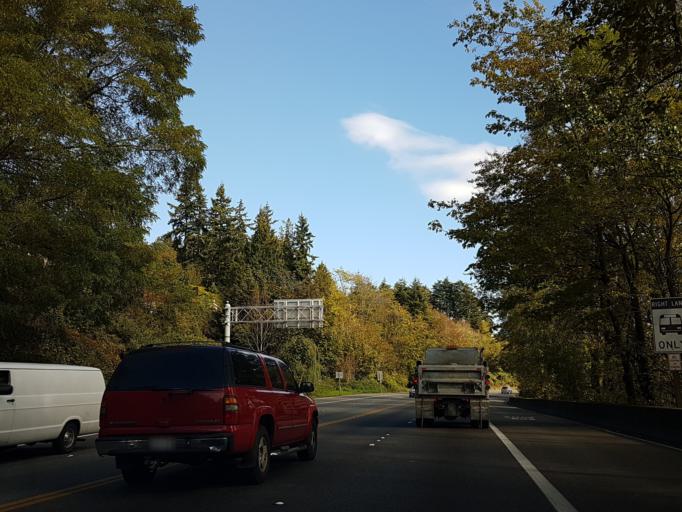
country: US
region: Washington
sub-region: King County
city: Lake Forest Park
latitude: 47.7560
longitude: -122.2718
